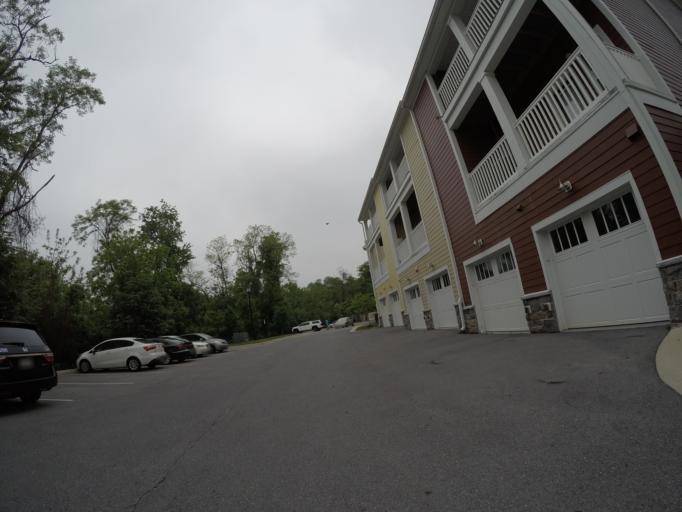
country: US
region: Maryland
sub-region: Howard County
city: Ellicott City
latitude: 39.2705
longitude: -76.8046
